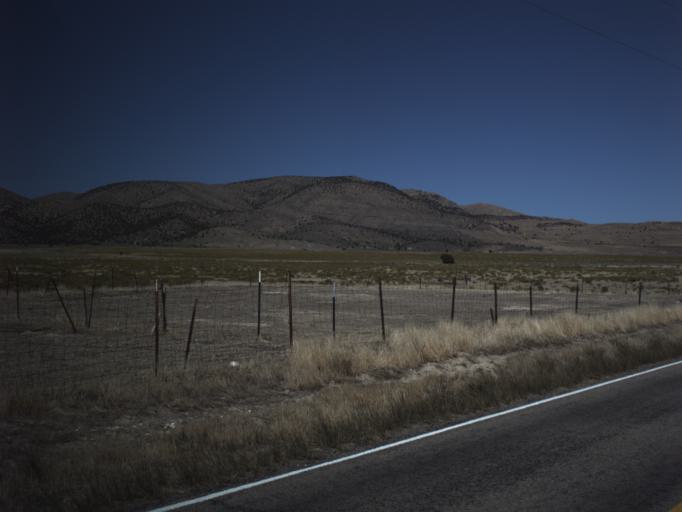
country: US
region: Utah
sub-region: Utah County
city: Eagle Mountain
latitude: 40.1626
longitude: -111.9483
